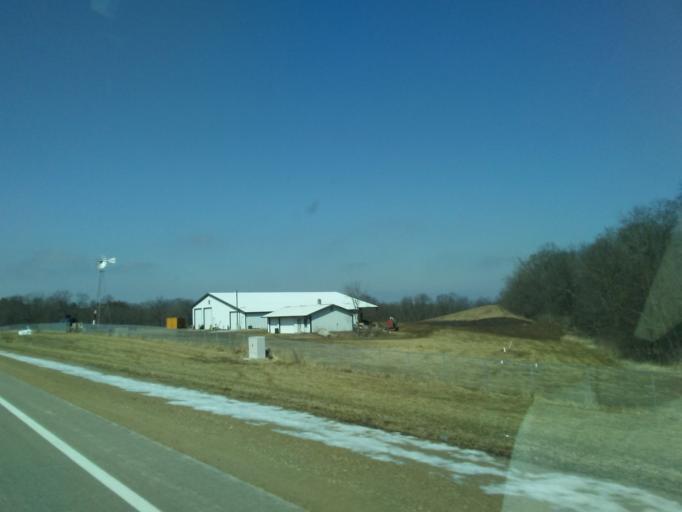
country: US
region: Wisconsin
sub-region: La Crosse County
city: La Crosse
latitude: 43.7204
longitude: -91.0808
